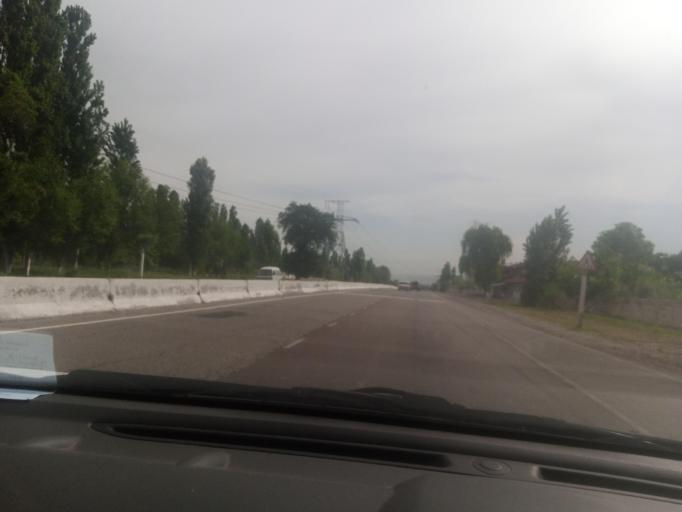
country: UZ
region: Toshkent
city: Angren
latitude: 40.9860
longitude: 70.0317
